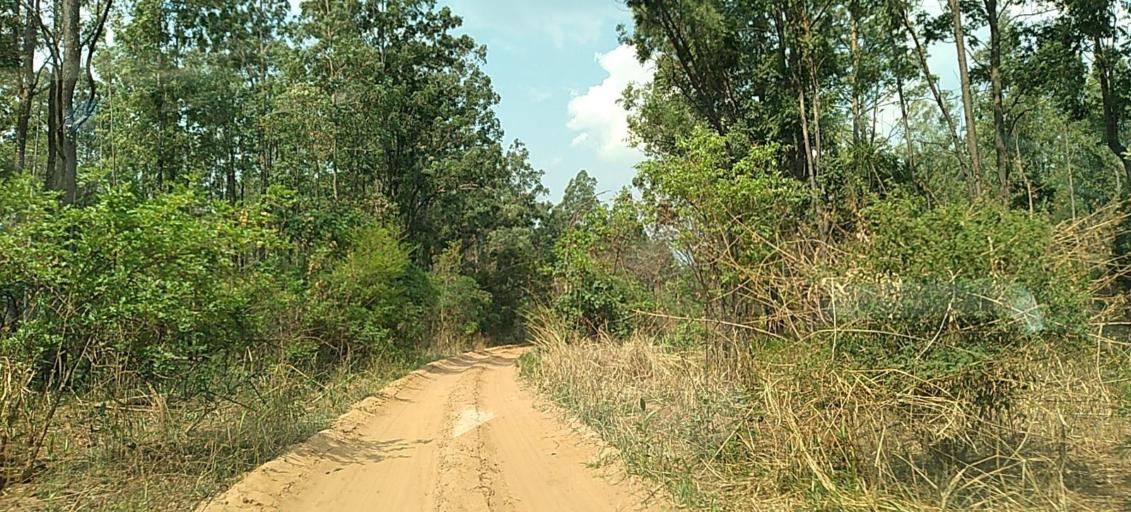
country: ZM
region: Copperbelt
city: Chingola
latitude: -12.7401
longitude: 27.7617
